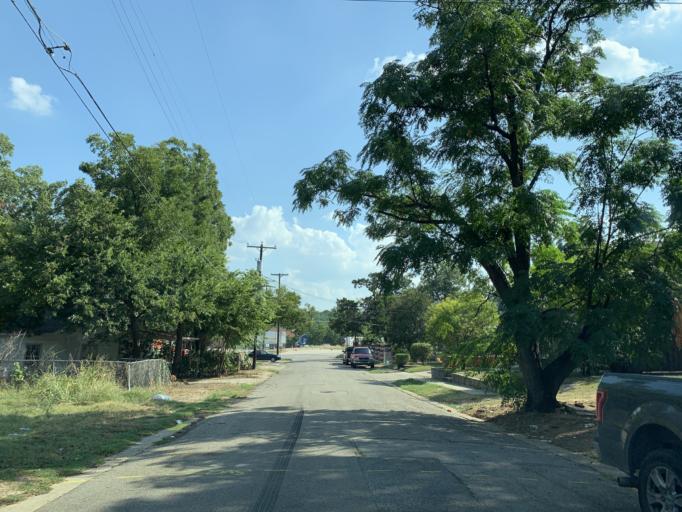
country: US
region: Texas
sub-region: Dallas County
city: Dallas
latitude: 32.7456
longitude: -96.8084
